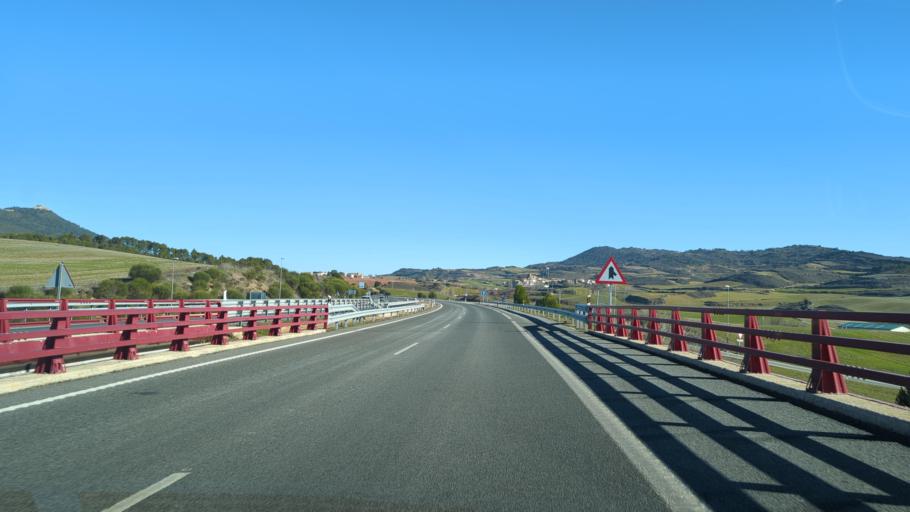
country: ES
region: Navarre
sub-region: Provincia de Navarra
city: Arroniz
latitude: 42.6003
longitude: -2.1205
